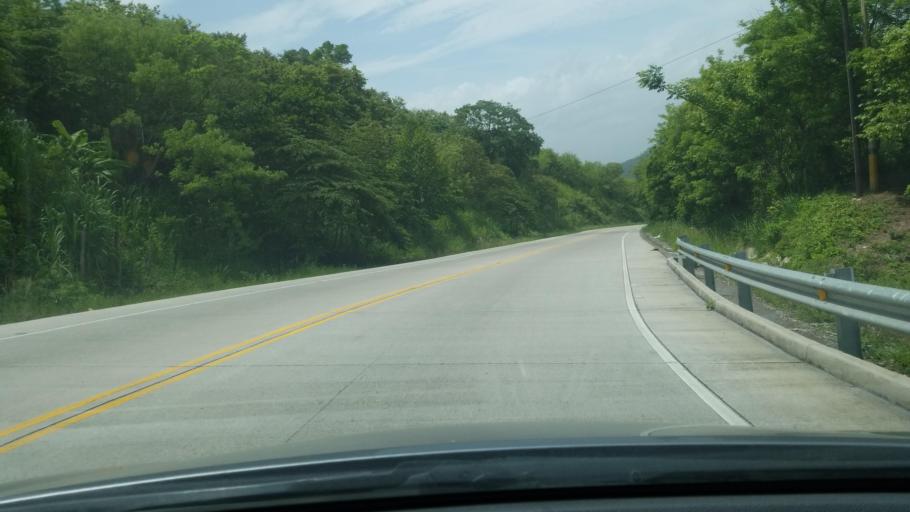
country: HN
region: Copan
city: Veracruz
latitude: 14.9113
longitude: -88.7526
